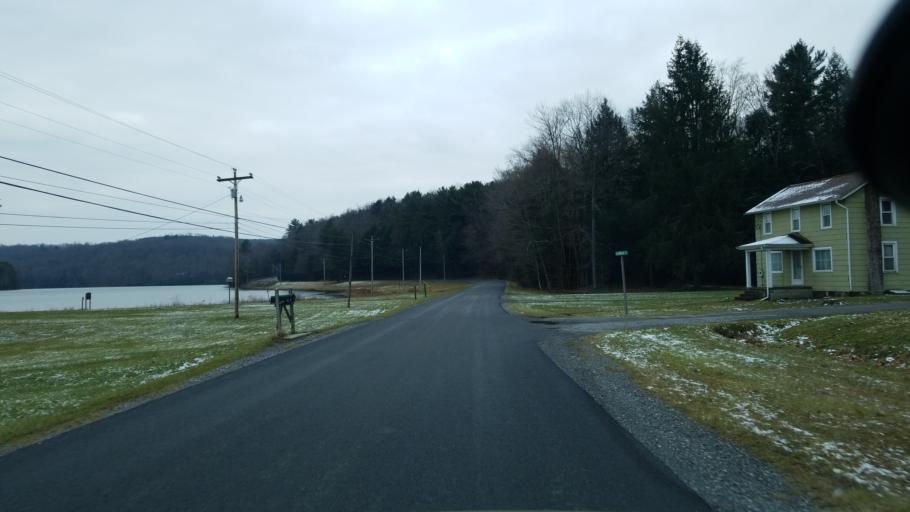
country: US
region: Pennsylvania
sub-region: Clearfield County
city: Treasure Lake
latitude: 41.1019
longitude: -78.6409
